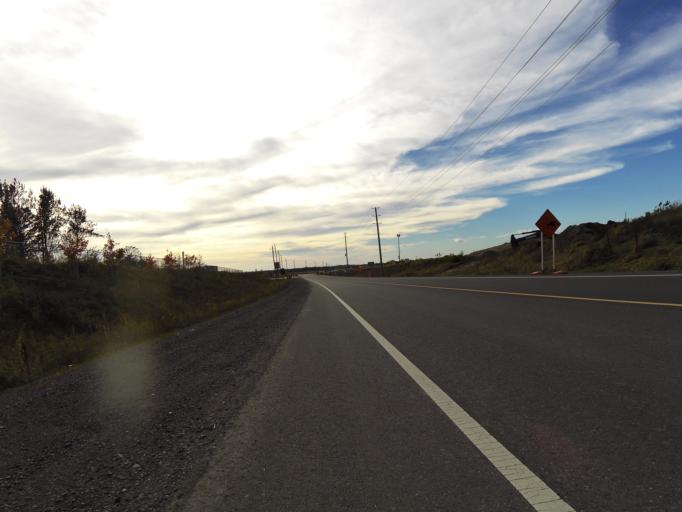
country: CA
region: Ontario
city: Oshawa
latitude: 43.8805
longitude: -78.7409
